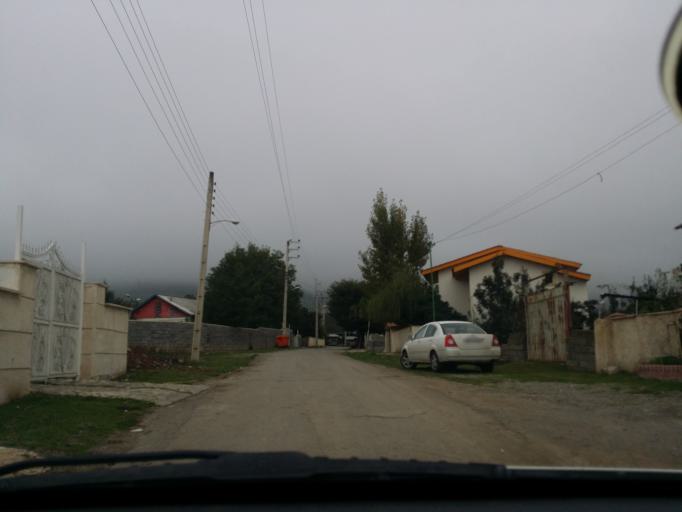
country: IR
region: Mazandaran
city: Chalus
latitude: 36.5114
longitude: 51.2264
